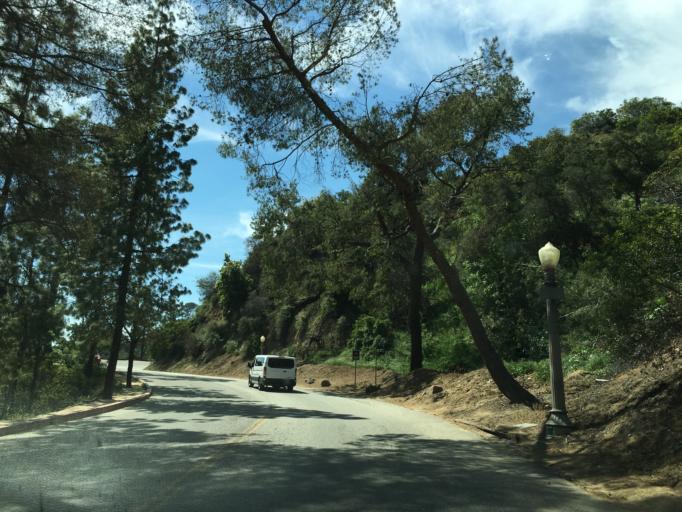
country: US
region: California
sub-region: Los Angeles County
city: Hollywood
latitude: 34.1242
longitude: -118.2977
